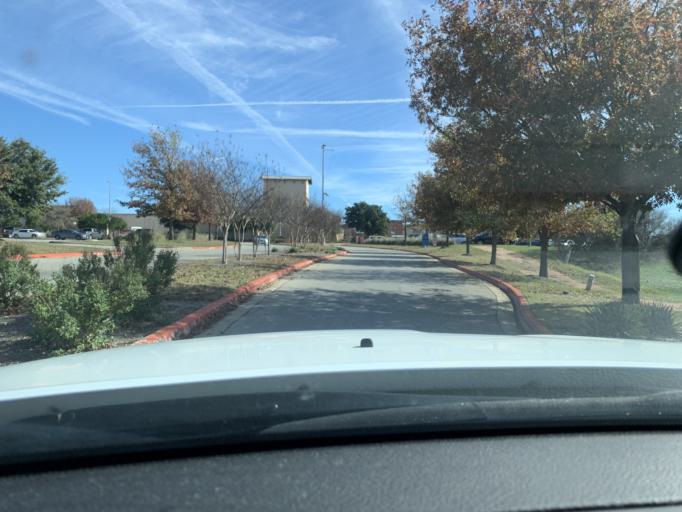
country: US
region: Texas
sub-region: Williamson County
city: Round Rock
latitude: 30.5649
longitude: -97.6918
